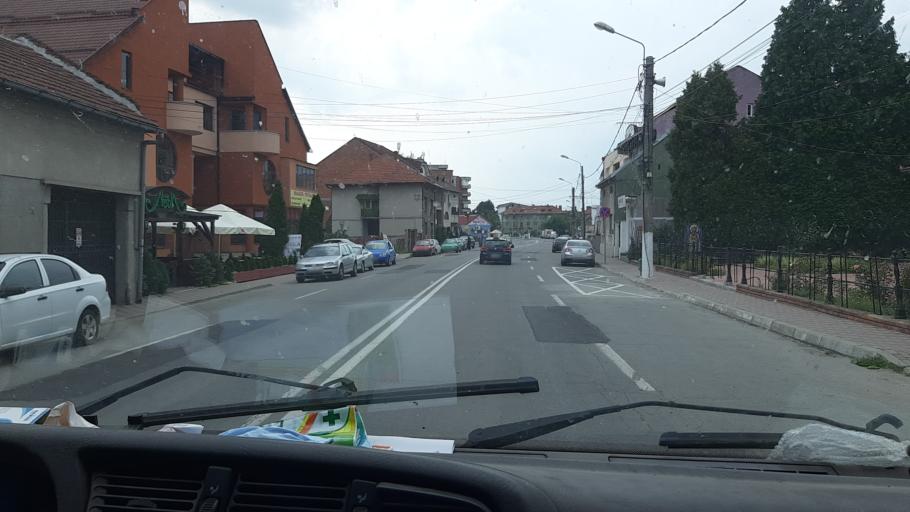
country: RO
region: Timis
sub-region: Municipiul Lugoj
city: Lugoj
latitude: 45.6955
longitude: 21.9009
